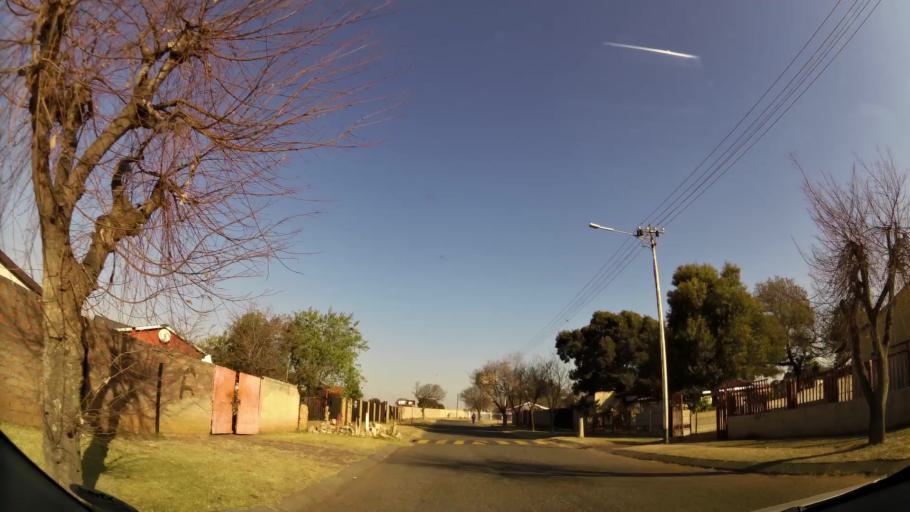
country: ZA
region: Gauteng
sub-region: West Rand District Municipality
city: Randfontein
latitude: -26.1992
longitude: 27.7006
